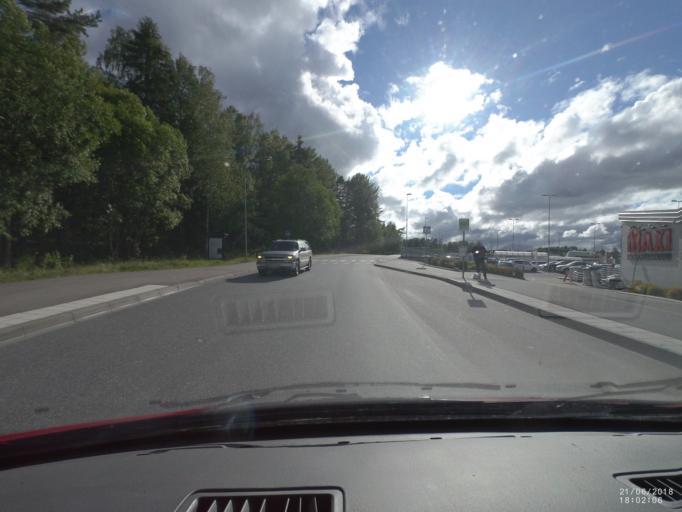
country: SE
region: Soedermanland
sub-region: Nykopings Kommun
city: Nykoping
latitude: 58.7699
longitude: 17.0218
